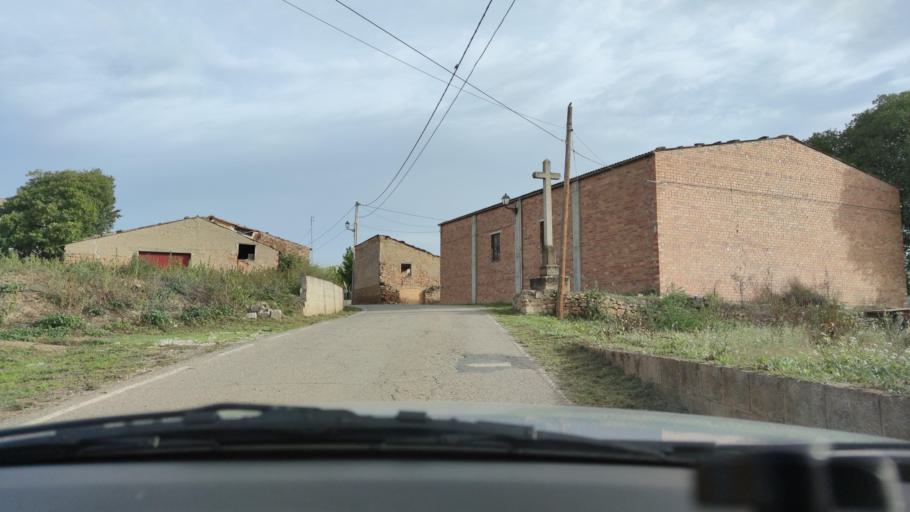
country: ES
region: Catalonia
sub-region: Provincia de Lleida
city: Artesa de Segre
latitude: 41.9155
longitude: 1.0140
